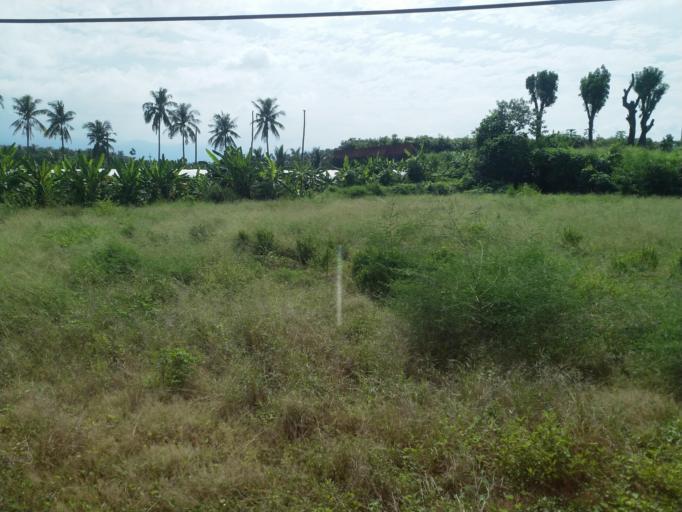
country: TW
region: Taiwan
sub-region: Pingtung
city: Pingtung
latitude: 22.8703
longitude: 120.4955
